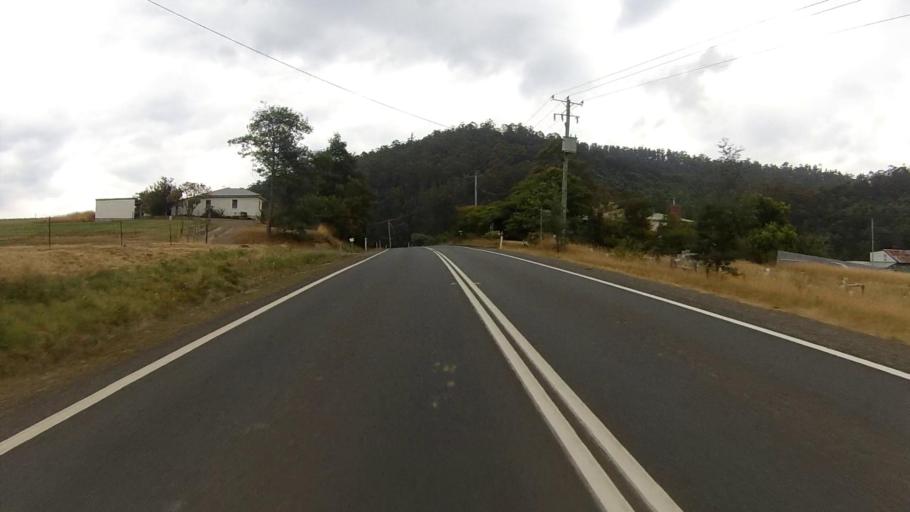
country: AU
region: Tasmania
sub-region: Huon Valley
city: Cygnet
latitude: -43.1427
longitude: 147.0640
